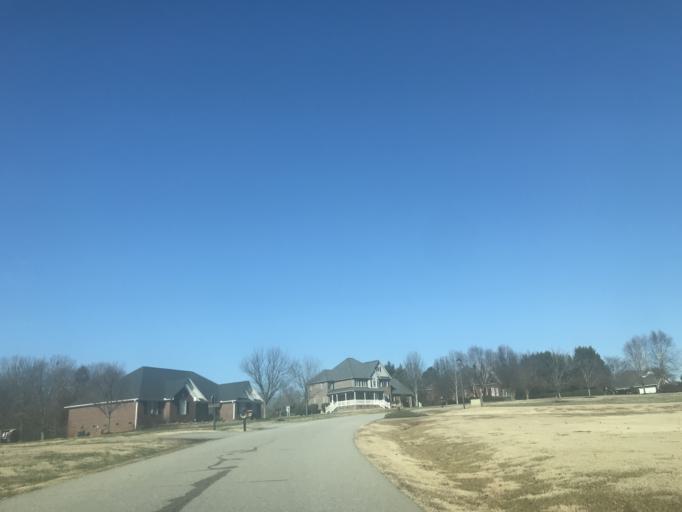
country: US
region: South Carolina
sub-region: Cherokee County
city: Gaffney
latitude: 35.1228
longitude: -81.6913
